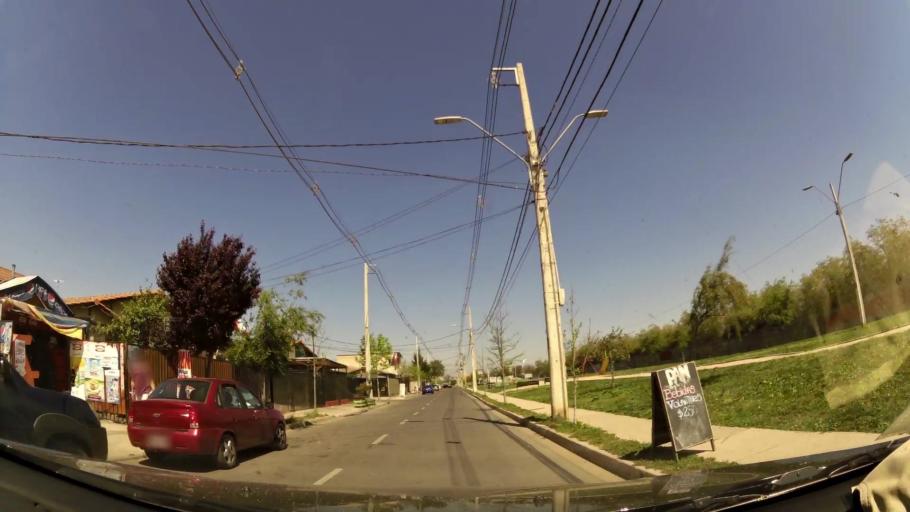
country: CL
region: Santiago Metropolitan
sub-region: Provincia de Santiago
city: Lo Prado
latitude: -33.3971
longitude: -70.7564
